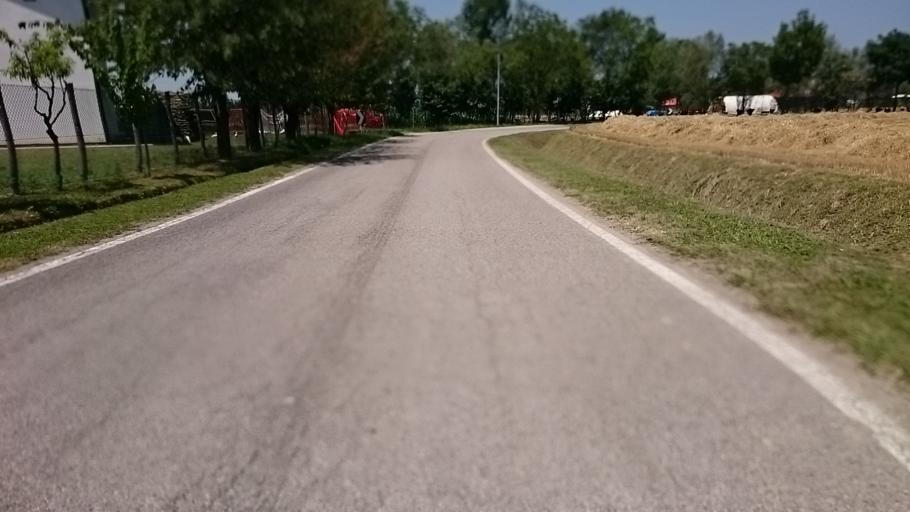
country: IT
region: Veneto
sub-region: Provincia di Venezia
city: Sant'Angelo
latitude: 45.5103
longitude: 12.0048
